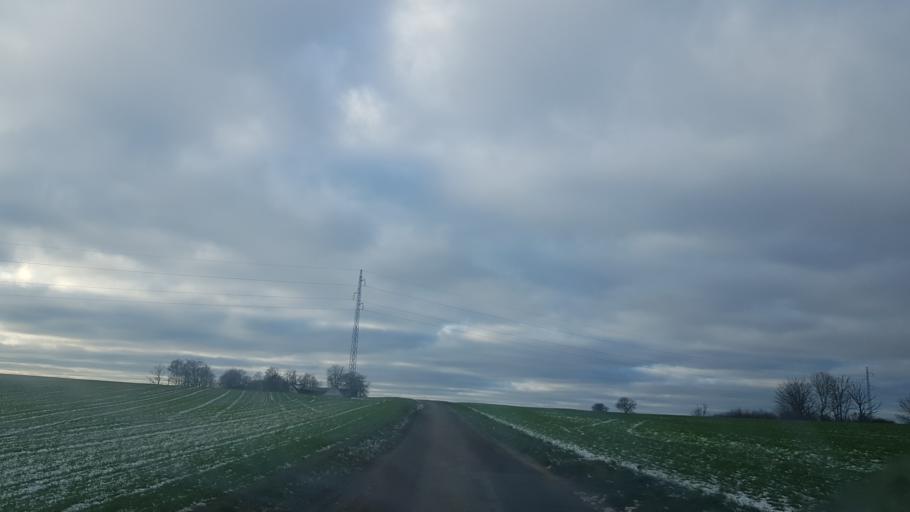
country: DK
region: Zealand
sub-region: Odsherred Kommune
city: Hojby
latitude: 55.9246
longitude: 11.5677
